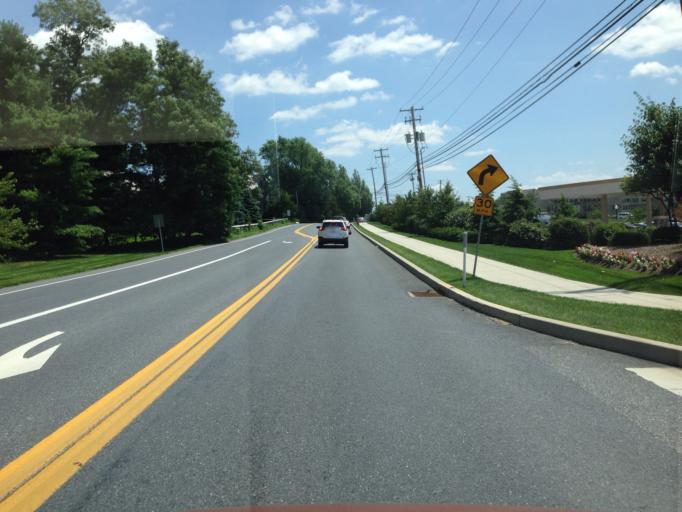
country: US
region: Pennsylvania
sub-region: Lancaster County
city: East Petersburg
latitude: 40.1070
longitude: -76.3333
